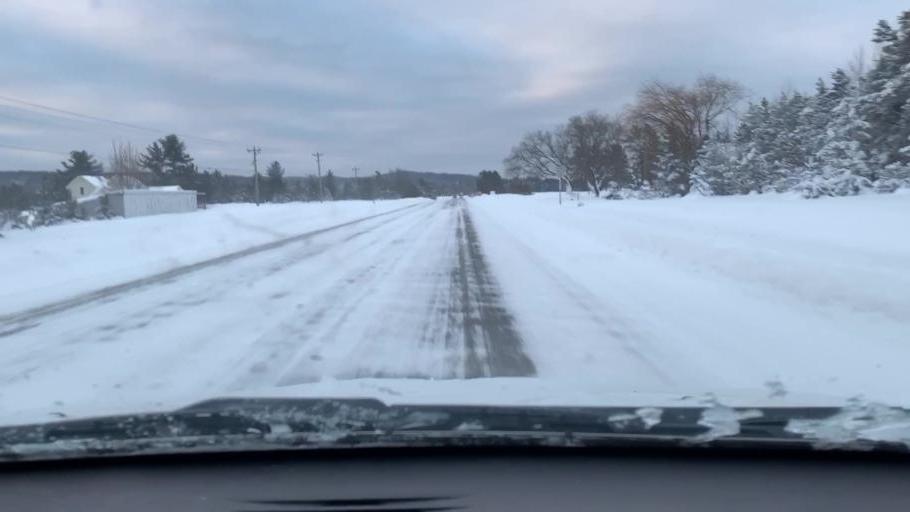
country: US
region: Michigan
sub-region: Antrim County
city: Mancelona
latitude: 44.9186
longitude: -85.0510
